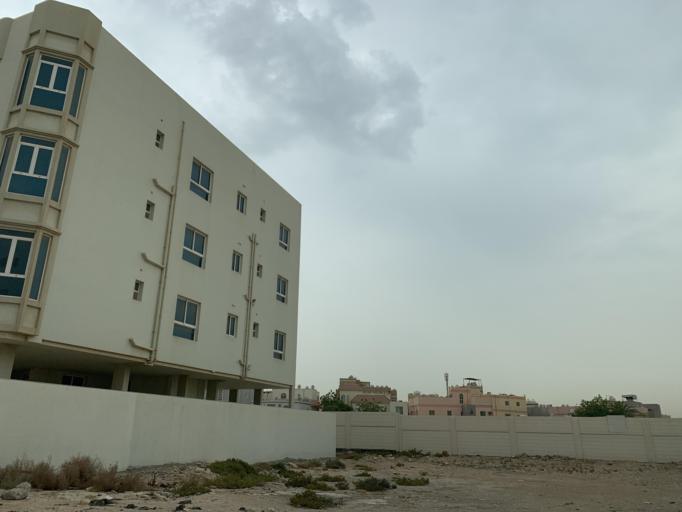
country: BH
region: Northern
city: Madinat `Isa
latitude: 26.1859
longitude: 50.4796
